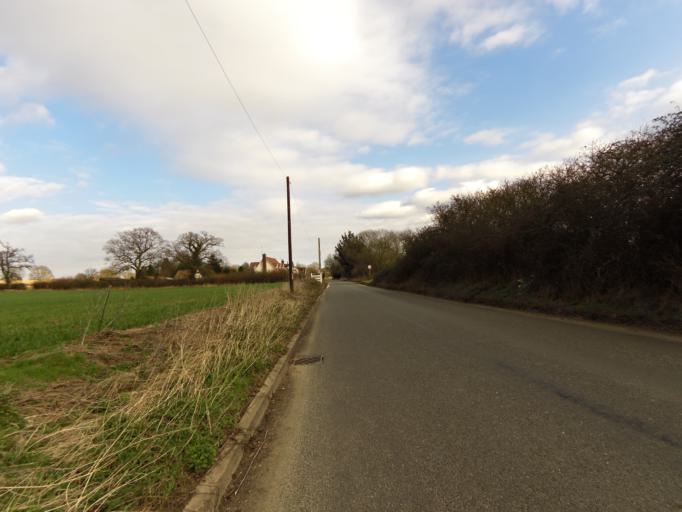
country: GB
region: England
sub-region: Suffolk
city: Ipswich
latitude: 52.0879
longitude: 1.1600
